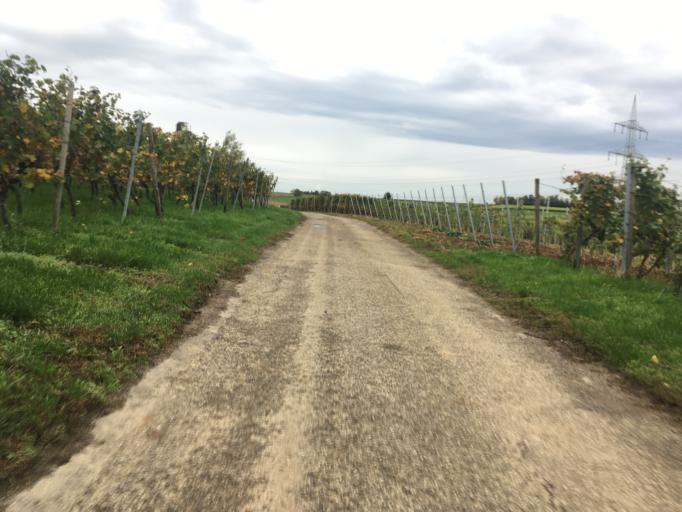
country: DE
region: Baden-Wuerttemberg
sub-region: Regierungsbezirk Stuttgart
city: Talheim
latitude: 49.0768
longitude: 9.1897
